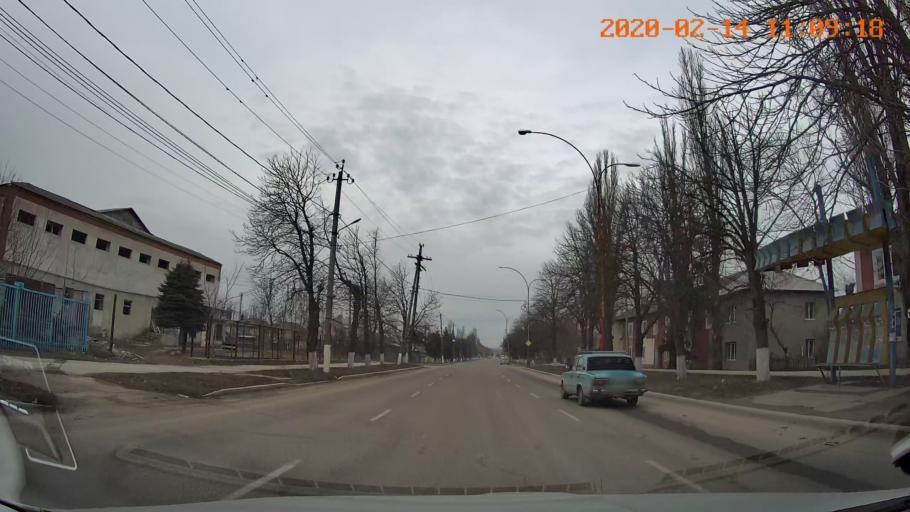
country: MD
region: Raionul Edinet
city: Edinet
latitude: 48.1772
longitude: 27.2952
